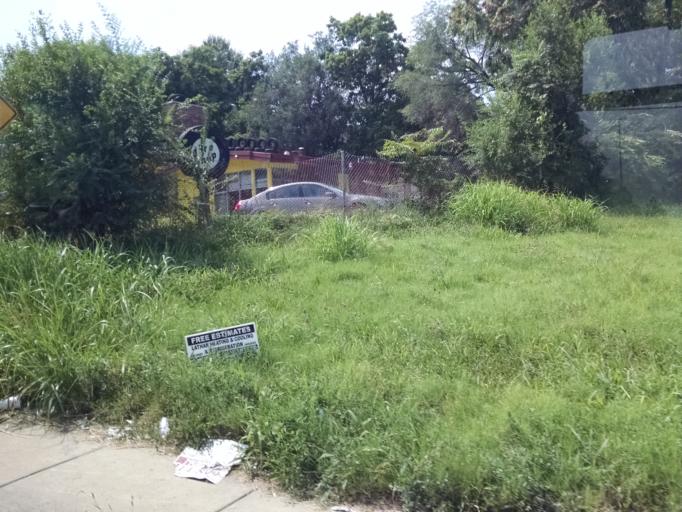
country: US
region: Illinois
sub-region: Madison County
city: Venice
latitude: 38.6728
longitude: -90.2050
